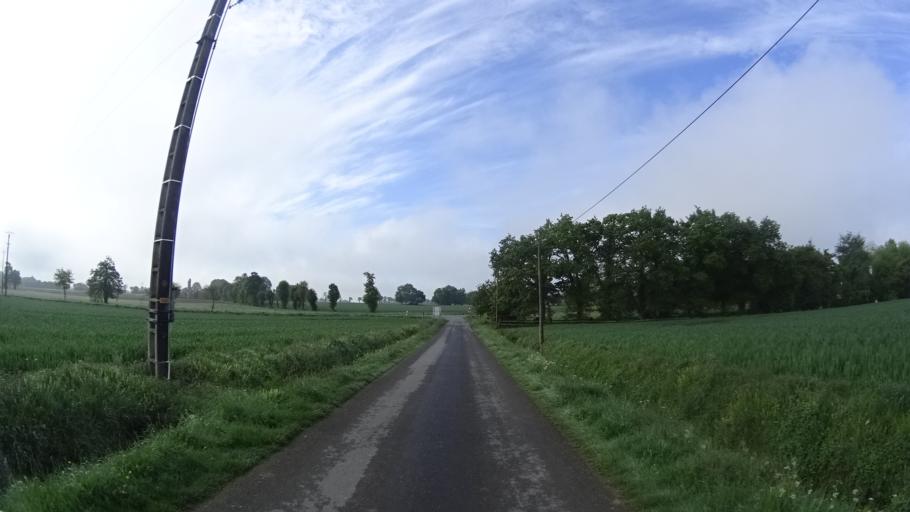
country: FR
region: Brittany
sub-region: Departement d'Ille-et-Vilaine
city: Mordelles
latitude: 48.0835
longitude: -1.8205
